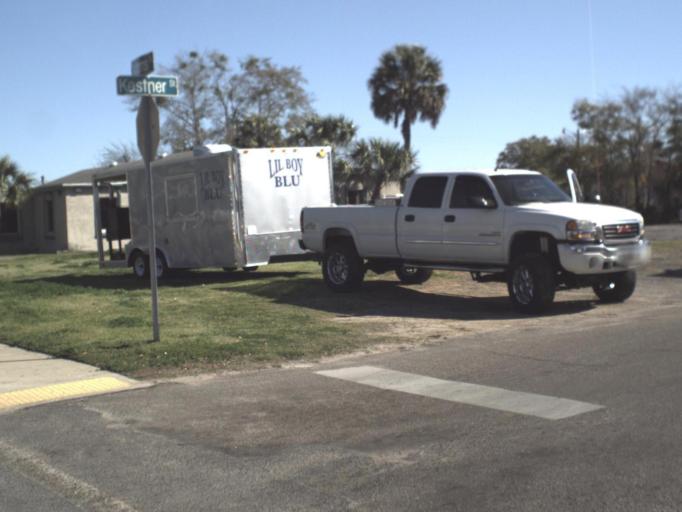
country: US
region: Florida
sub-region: Leon County
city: Tallahassee
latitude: 30.4215
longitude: -84.2820
